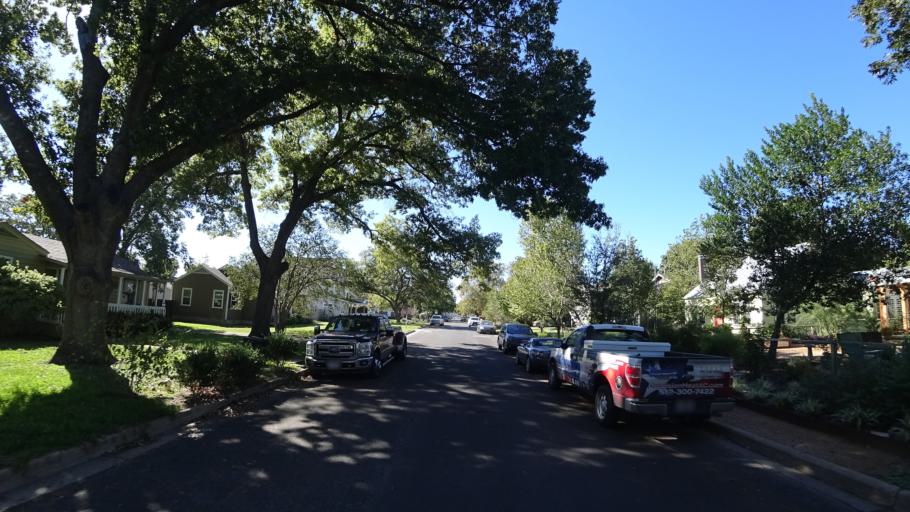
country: US
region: Texas
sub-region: Travis County
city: Austin
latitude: 30.3093
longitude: -97.7535
